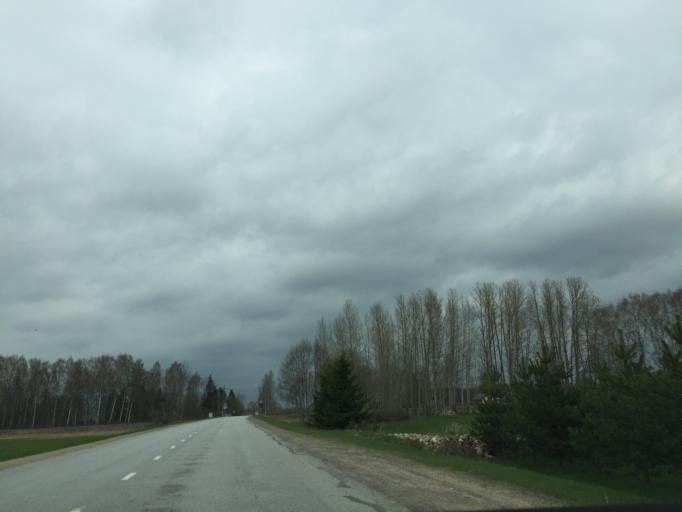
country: EE
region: Tartu
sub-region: Noo vald
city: Noo
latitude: 58.2785
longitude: 26.5289
